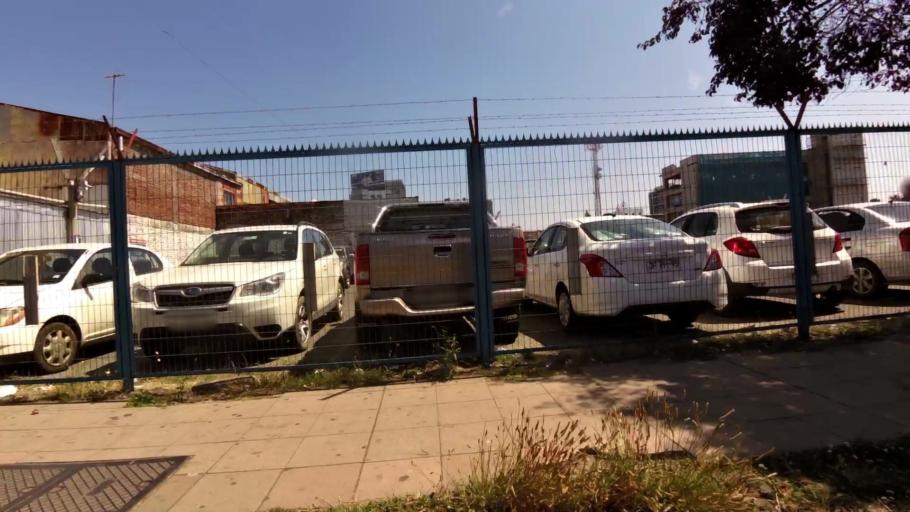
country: CL
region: Biobio
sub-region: Provincia de Concepcion
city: Concepcion
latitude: -36.8224
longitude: -73.0508
